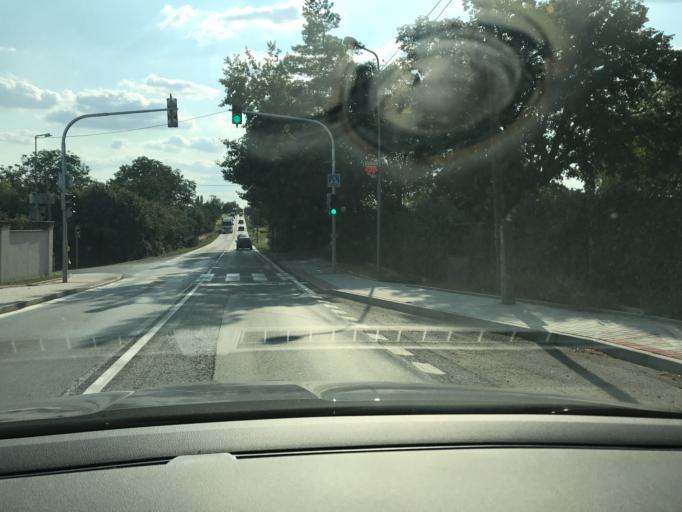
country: CZ
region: Central Bohemia
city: Brandysek
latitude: 50.2543
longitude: 14.1607
